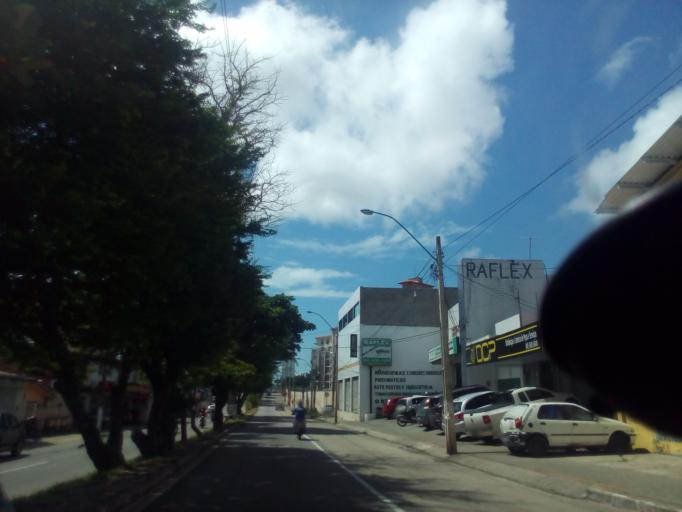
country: BR
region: Rio Grande do Norte
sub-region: Natal
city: Natal
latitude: -5.8227
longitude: -35.2294
